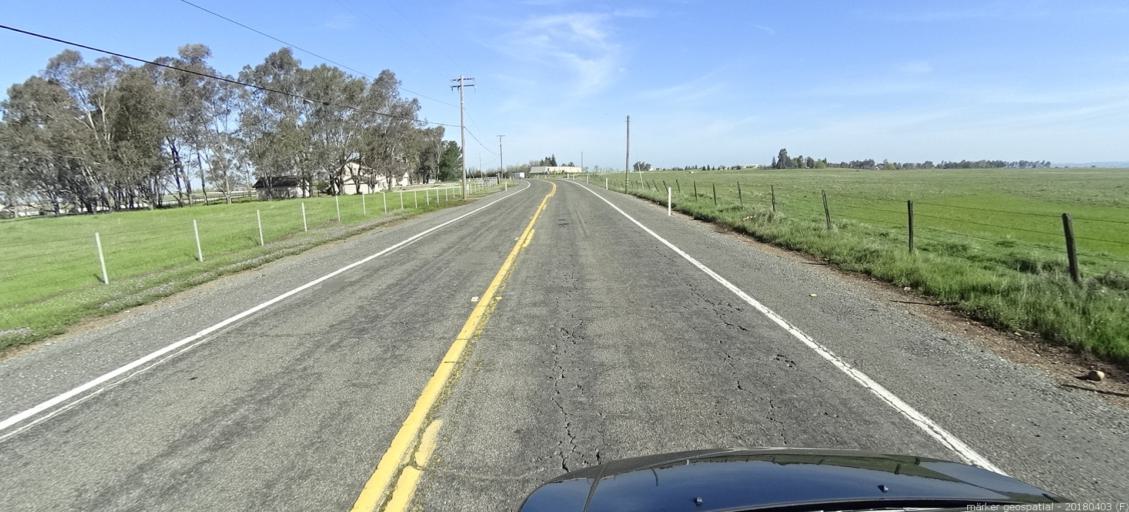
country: US
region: California
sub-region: Sacramento County
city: Clay
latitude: 38.4112
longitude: -121.1750
